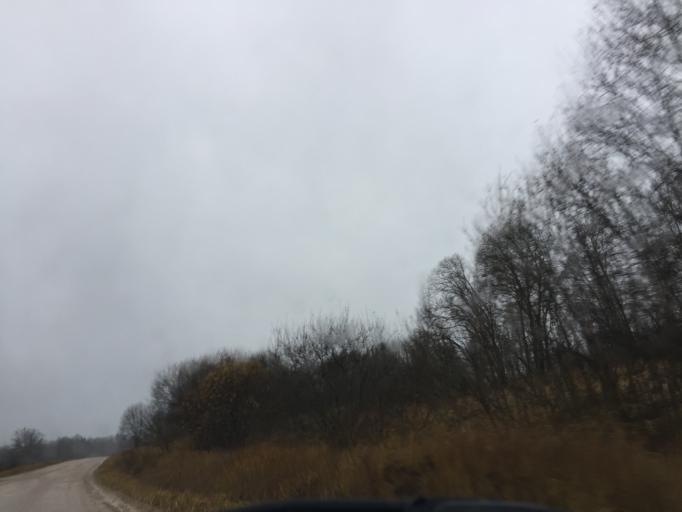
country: LV
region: Salas
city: Sala
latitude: 56.4939
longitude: 25.6824
